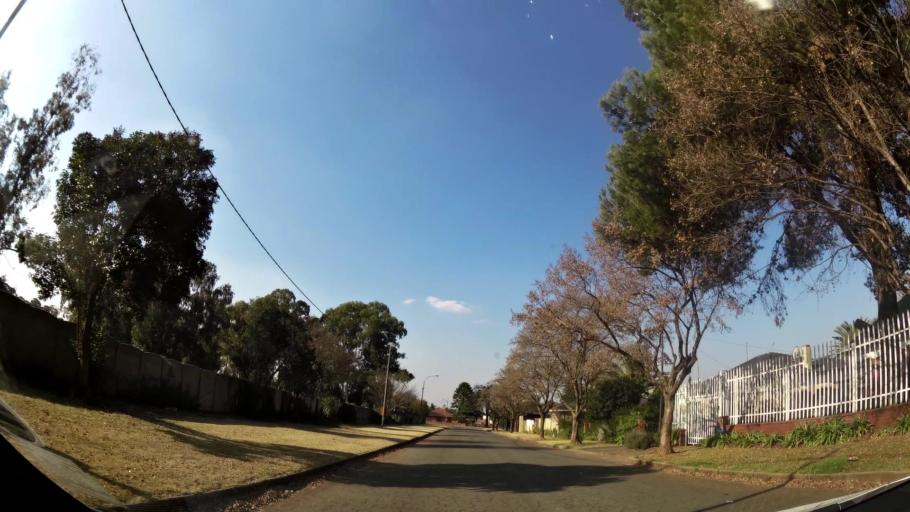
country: ZA
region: Gauteng
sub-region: Ekurhuleni Metropolitan Municipality
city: Brakpan
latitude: -26.2299
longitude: 28.3570
